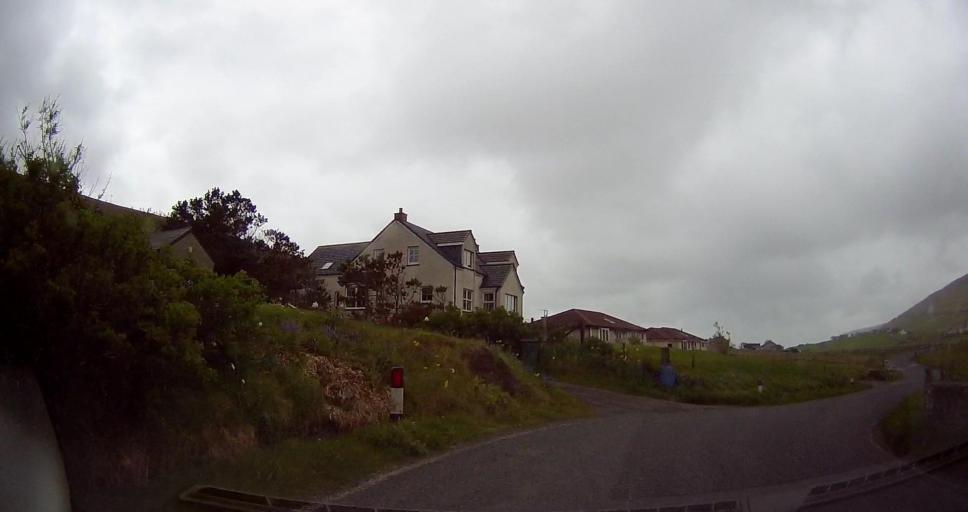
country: GB
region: Scotland
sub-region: Shetland Islands
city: Lerwick
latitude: 60.2548
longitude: -1.2895
